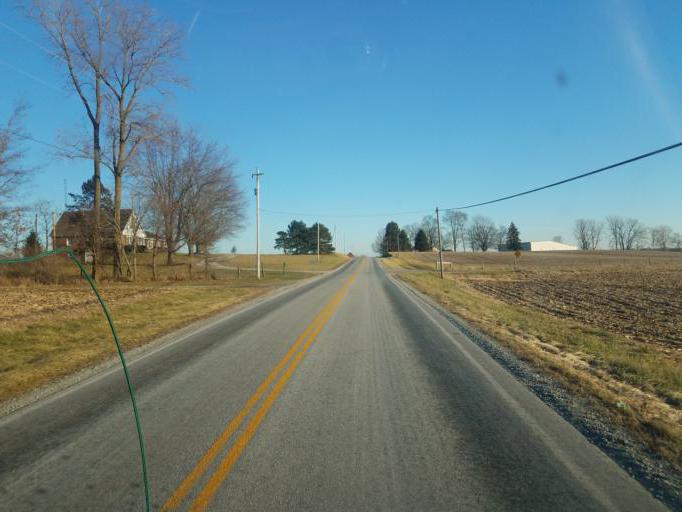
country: US
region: Ohio
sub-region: Hardin County
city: Kenton
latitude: 40.6350
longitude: -83.5531
